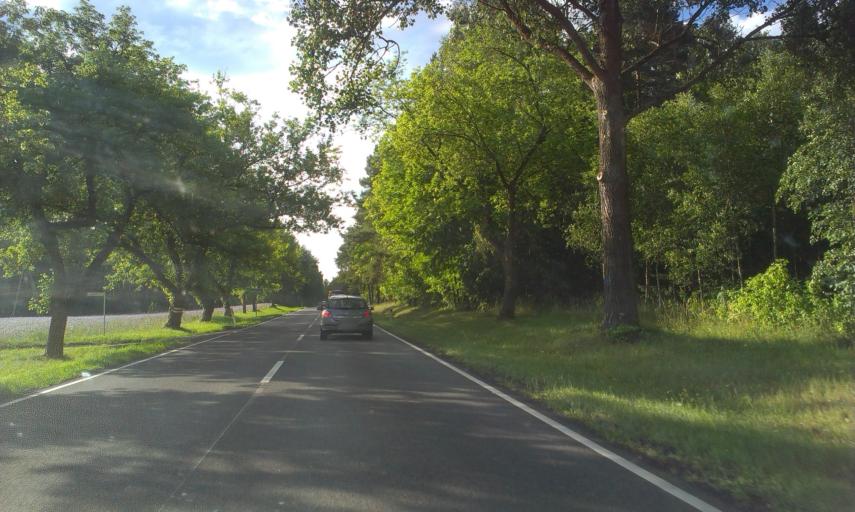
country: PL
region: Greater Poland Voivodeship
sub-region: Powiat zlotowski
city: Okonek
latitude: 53.4942
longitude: 16.8610
